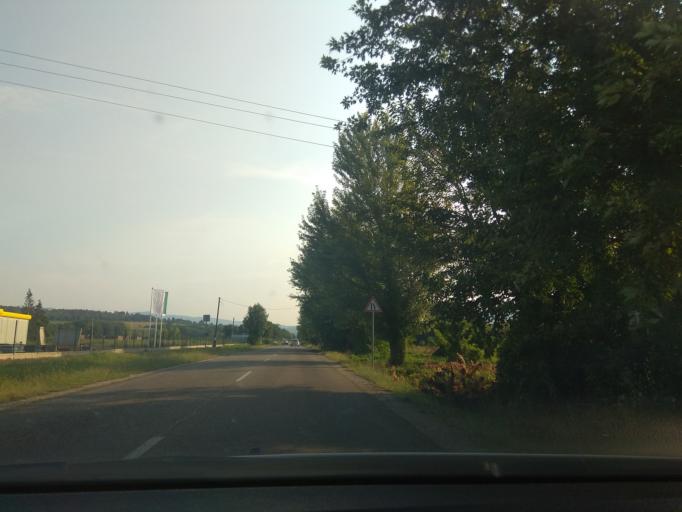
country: HU
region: Heves
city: Felsotarkany
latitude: 47.9459
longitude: 20.3806
